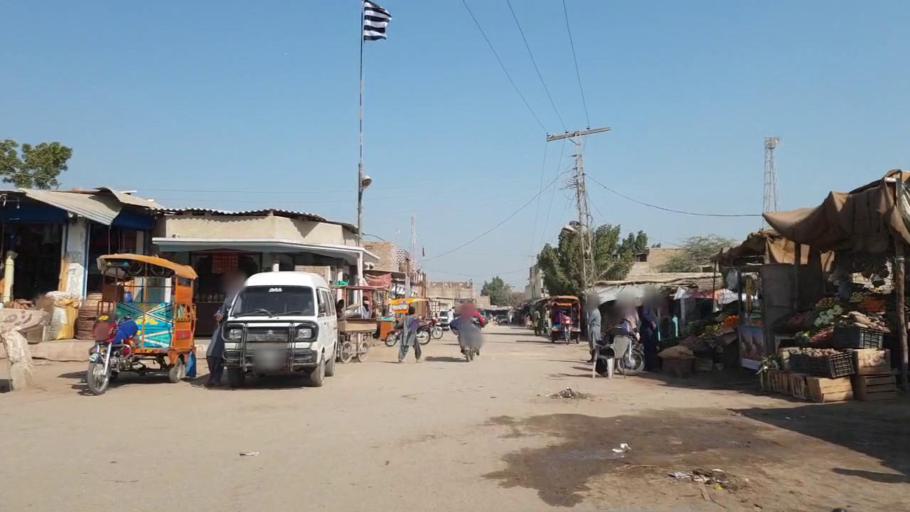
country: PK
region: Sindh
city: Tando Adam
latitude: 25.6287
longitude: 68.5946
